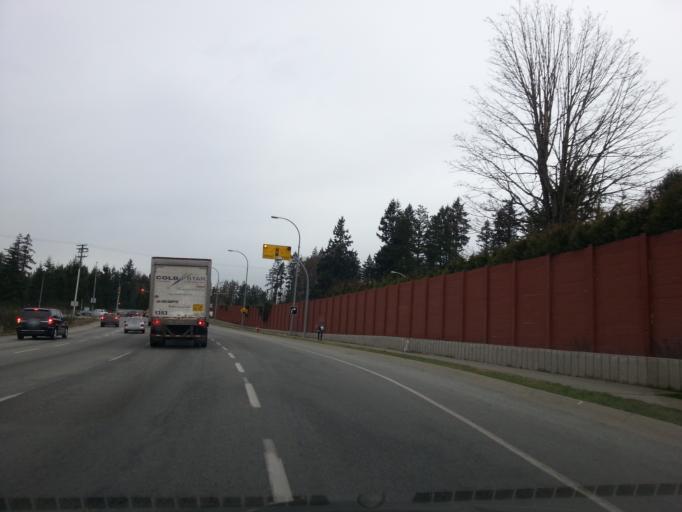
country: CA
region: British Columbia
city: Surrey
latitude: 49.1052
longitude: -122.8300
